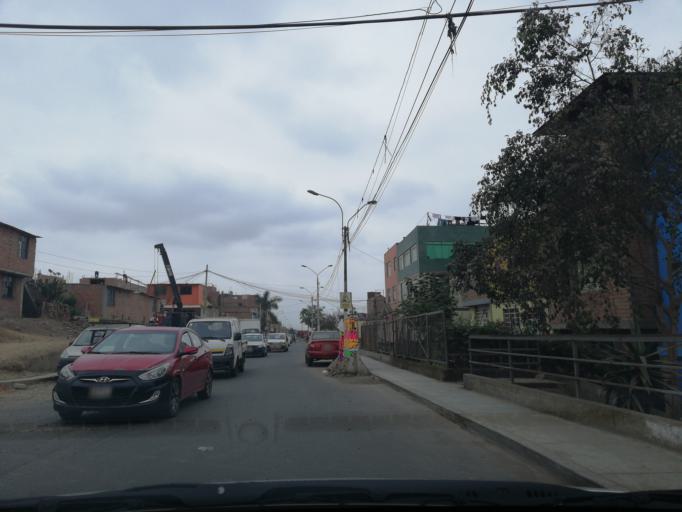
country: PE
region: Lima
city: Lima
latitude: -12.0374
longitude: -77.0512
